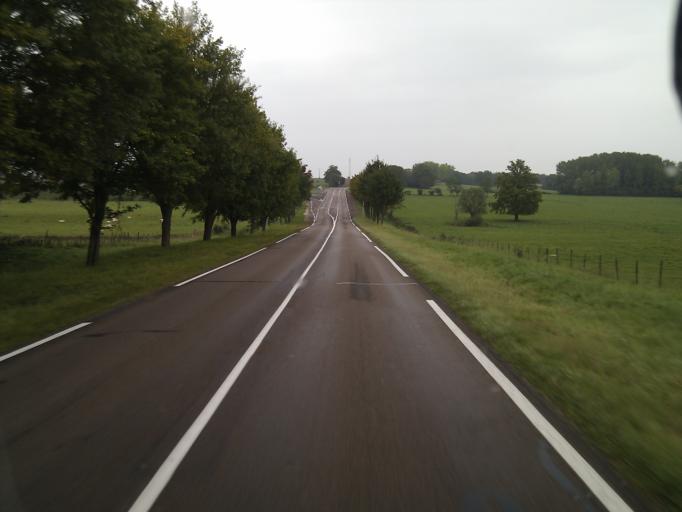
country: FR
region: Bourgogne
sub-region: Departement de la Cote-d'Or
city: Semur-en-Auxois
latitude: 47.4342
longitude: 4.3123
